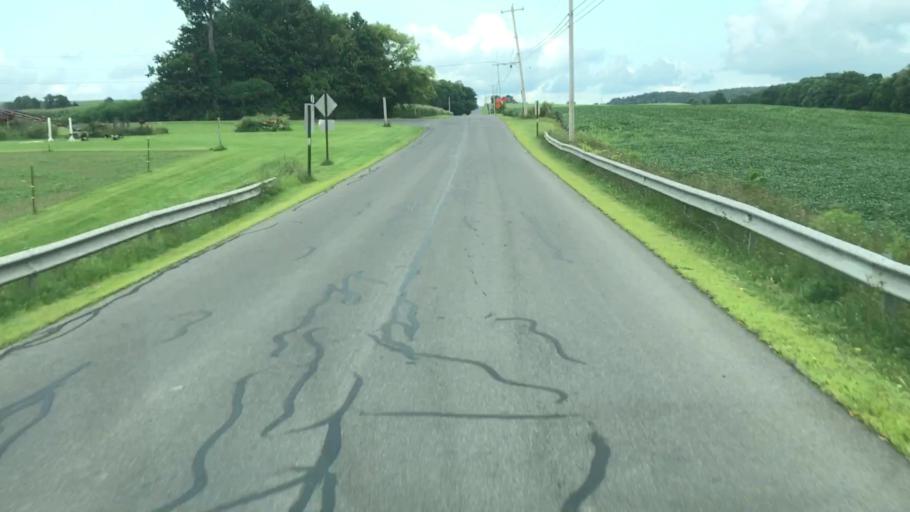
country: US
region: New York
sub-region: Onondaga County
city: Elbridge
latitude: 42.9849
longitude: -76.5077
